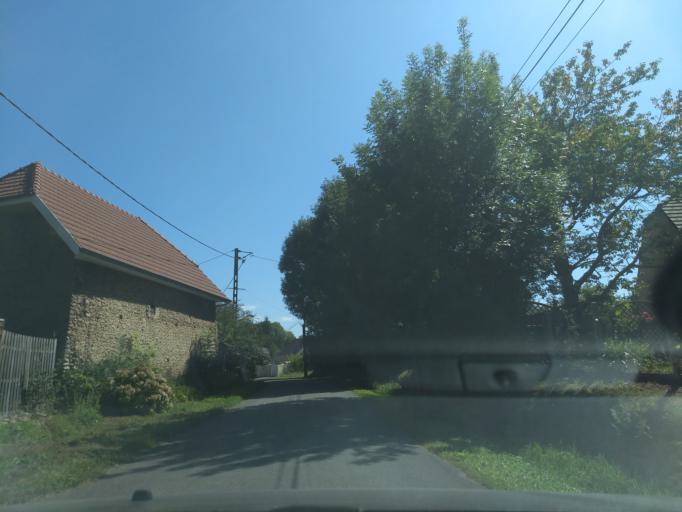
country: FR
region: Aquitaine
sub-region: Departement des Pyrenees-Atlantiques
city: Soumoulou
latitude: 43.2886
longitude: -0.1583
